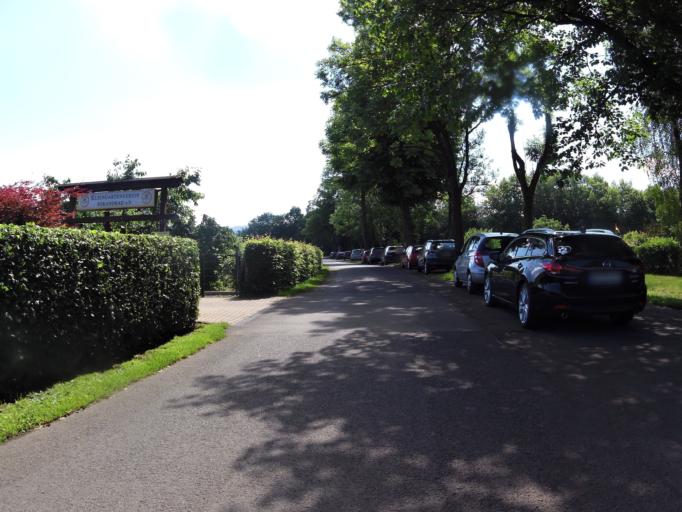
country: DE
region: Hesse
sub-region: Regierungsbezirk Kassel
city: Bad Hersfeld
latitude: 50.8570
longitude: 9.6986
